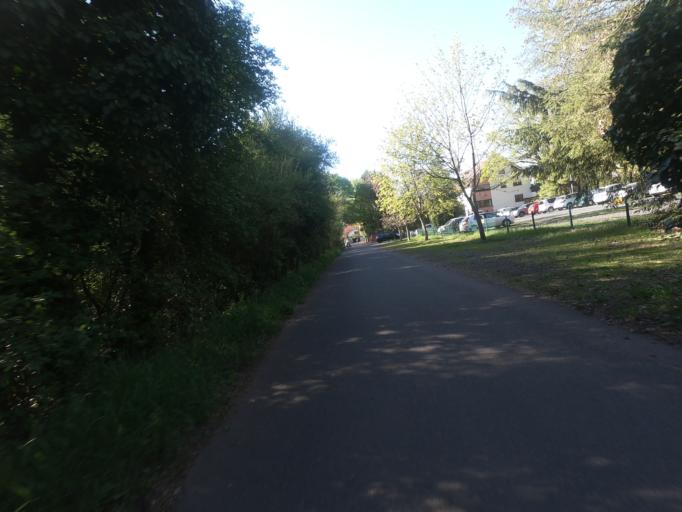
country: DE
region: Hesse
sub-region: Regierungsbezirk Darmstadt
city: Egelsbach
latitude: 49.9814
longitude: 8.6929
